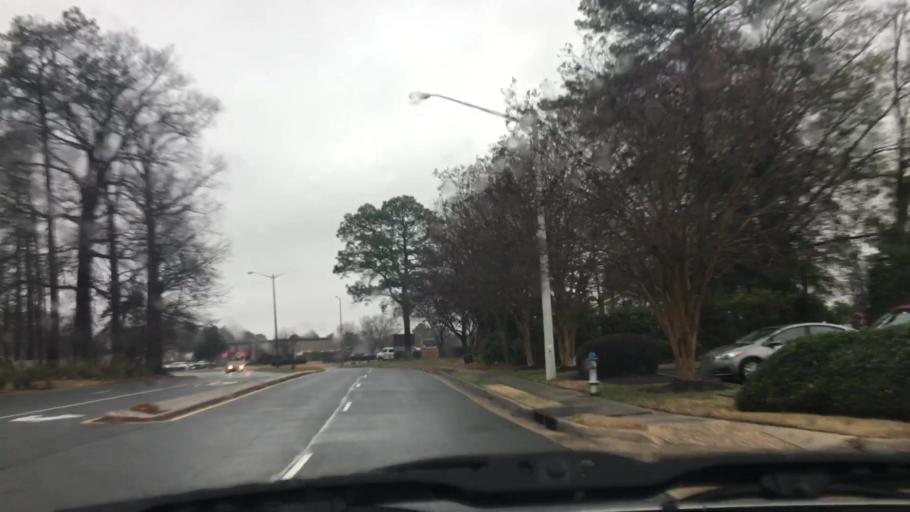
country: US
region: Virginia
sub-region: City of Chesapeake
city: Chesapeake
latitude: 36.7673
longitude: -76.2490
